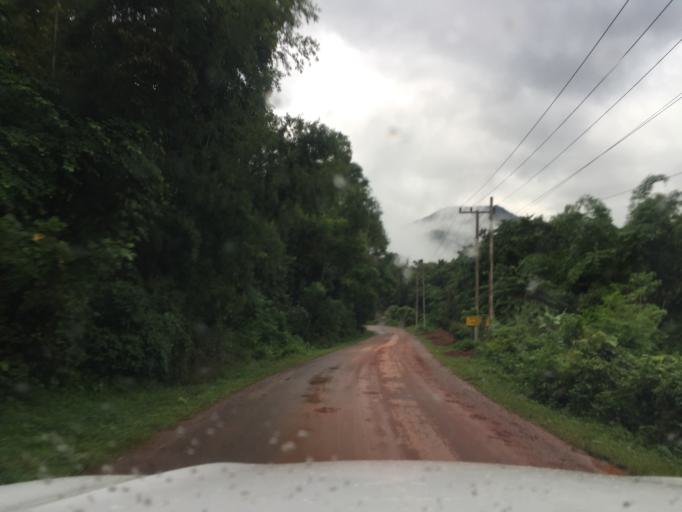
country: LA
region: Oudomxai
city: Muang La
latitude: 20.8403
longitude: 102.1038
